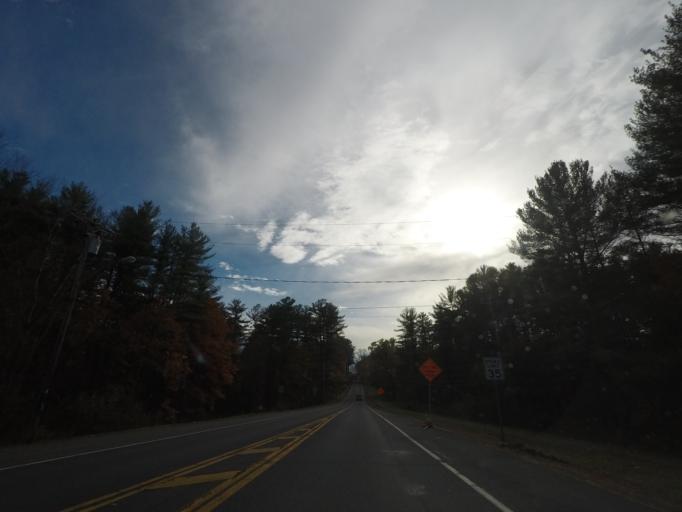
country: US
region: New York
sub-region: Albany County
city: Delmar
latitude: 42.6357
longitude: -73.8567
